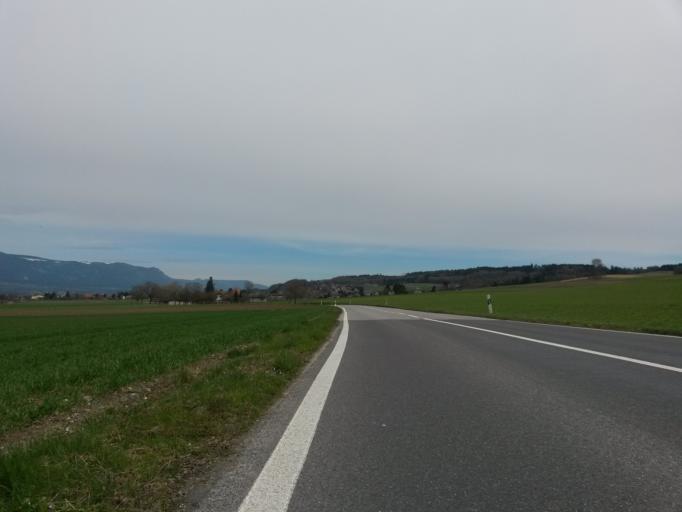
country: CH
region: Bern
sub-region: Biel/Bienne District
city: Lengnau
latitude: 47.1447
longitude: 7.3920
